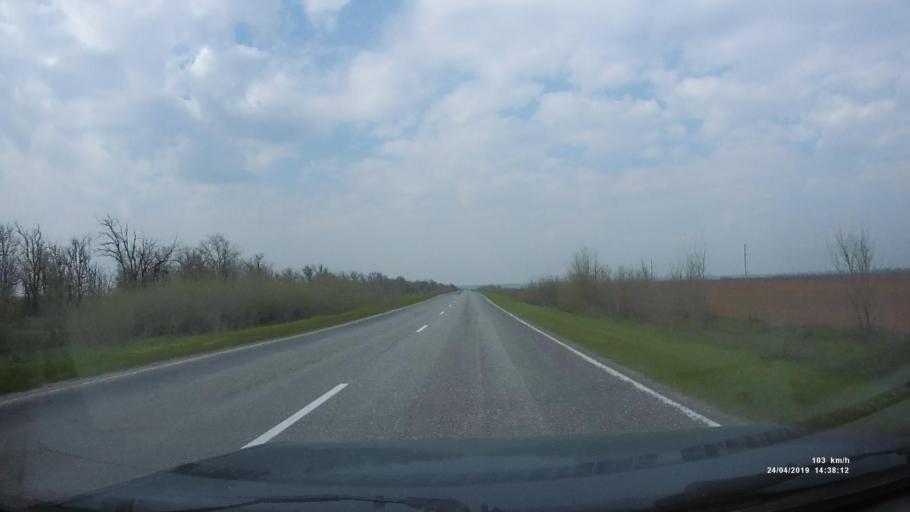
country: RU
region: Rostov
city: Remontnoye
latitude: 46.3977
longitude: 43.8861
